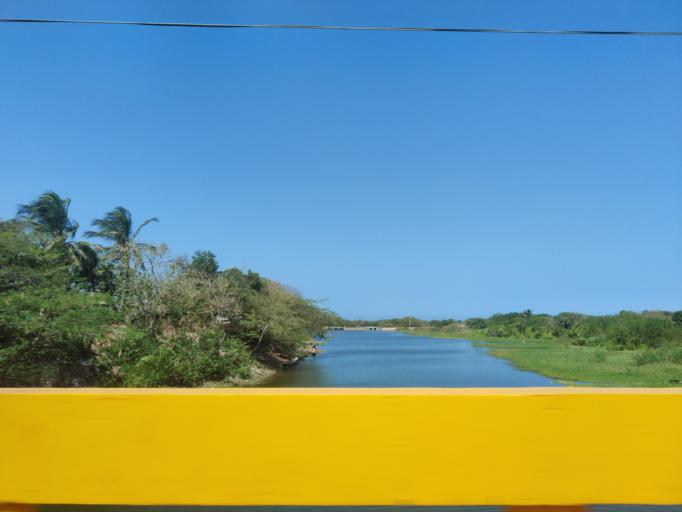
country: CO
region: Bolivar
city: Santa Catalina
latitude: 10.7391
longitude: -75.2604
